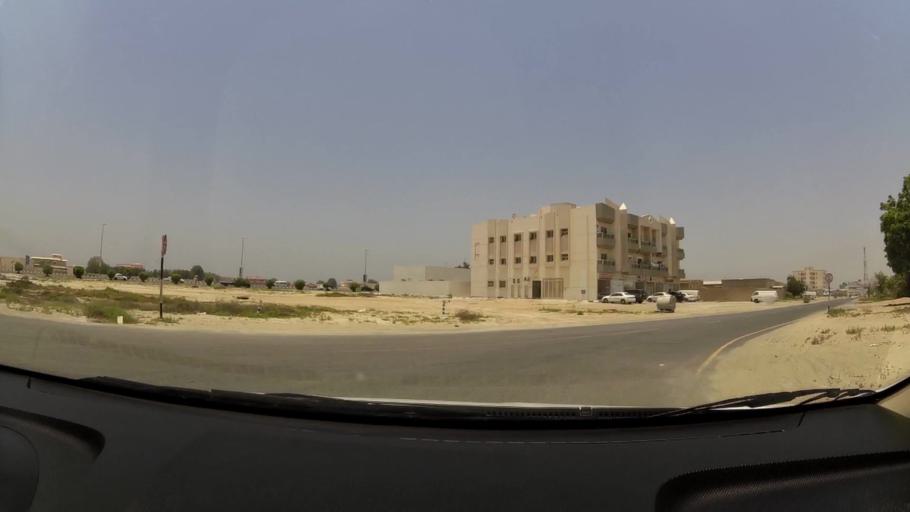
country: AE
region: Umm al Qaywayn
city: Umm al Qaywayn
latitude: 25.5324
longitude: 55.5394
